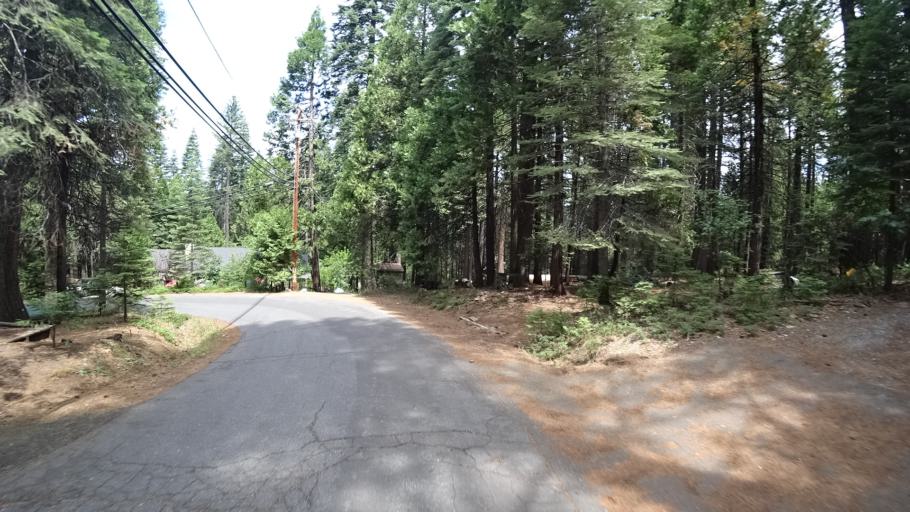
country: US
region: California
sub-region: Calaveras County
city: Arnold
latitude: 38.2556
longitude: -120.3452
